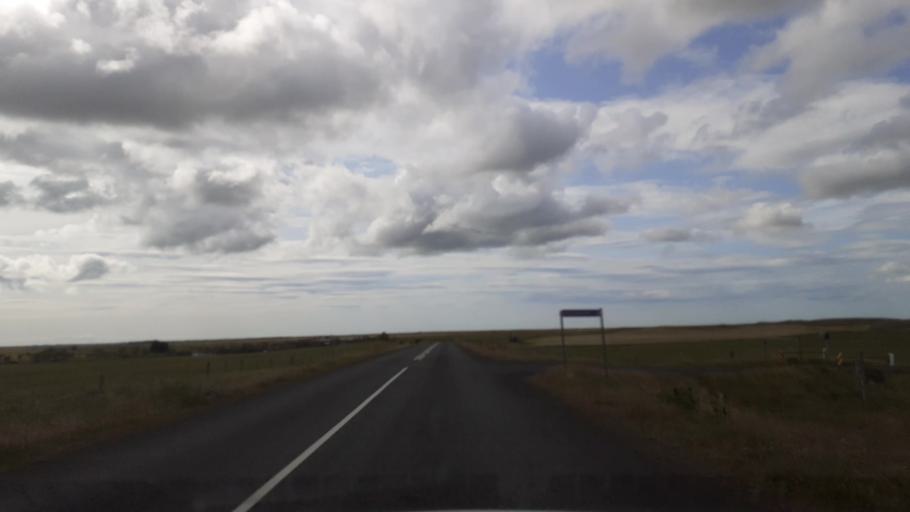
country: IS
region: South
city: Vestmannaeyjar
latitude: 63.8361
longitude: -20.4167
